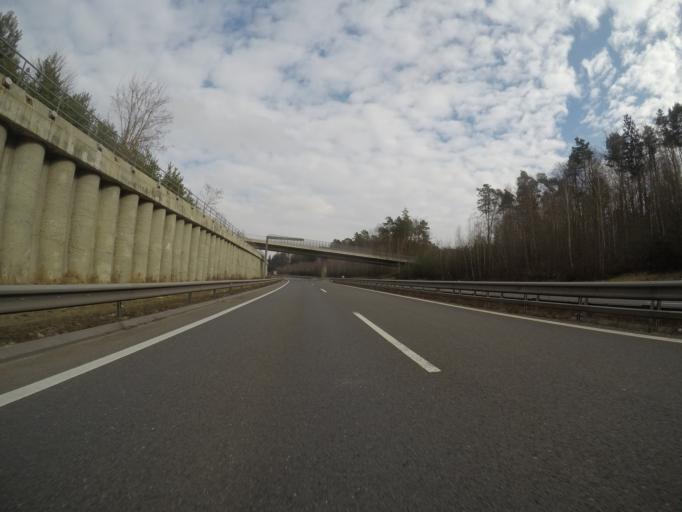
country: SI
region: Sveti Jurij
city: Sveti Jurij ob Scavnici
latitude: 46.5757
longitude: 16.0507
